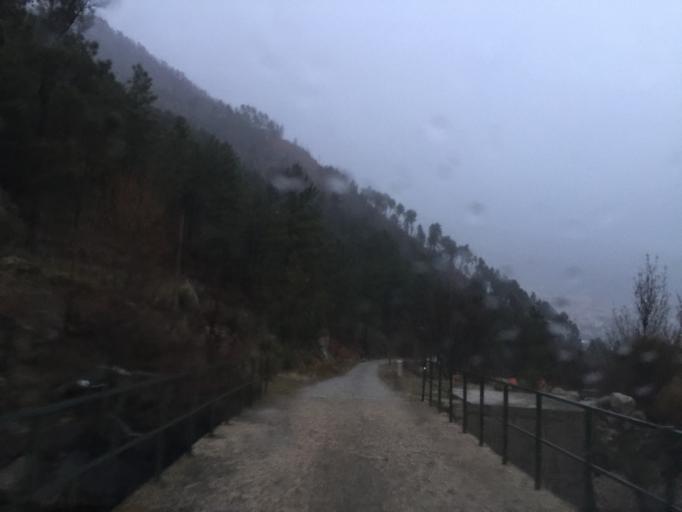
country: PT
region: Guarda
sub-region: Manteigas
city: Manteigas
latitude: 40.3821
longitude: -7.5480
